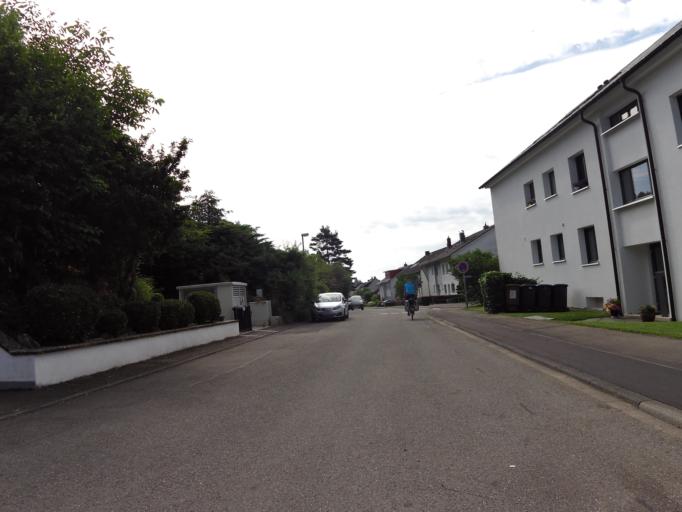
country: DE
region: Baden-Wuerttemberg
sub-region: Freiburg Region
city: Allensbach
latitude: 47.7216
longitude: 9.0539
